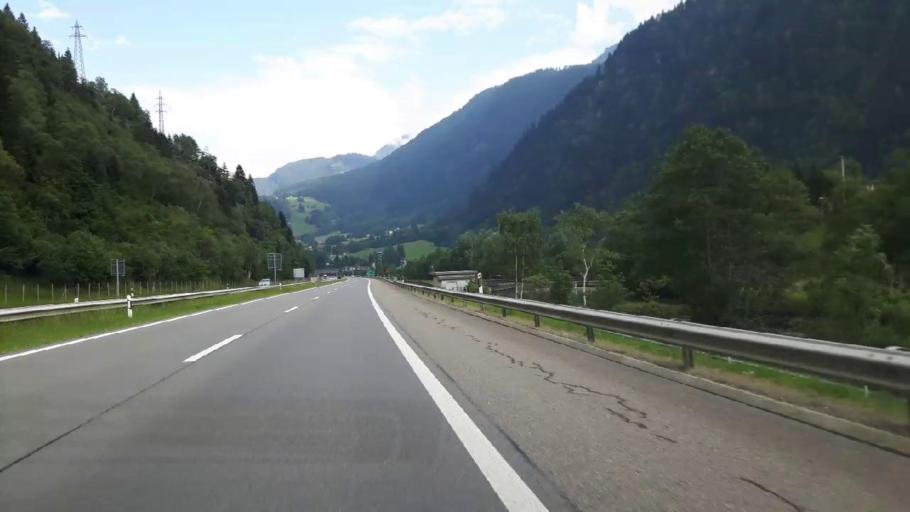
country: CH
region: Ticino
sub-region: Leventina District
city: Faido
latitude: 46.4967
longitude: 8.7337
